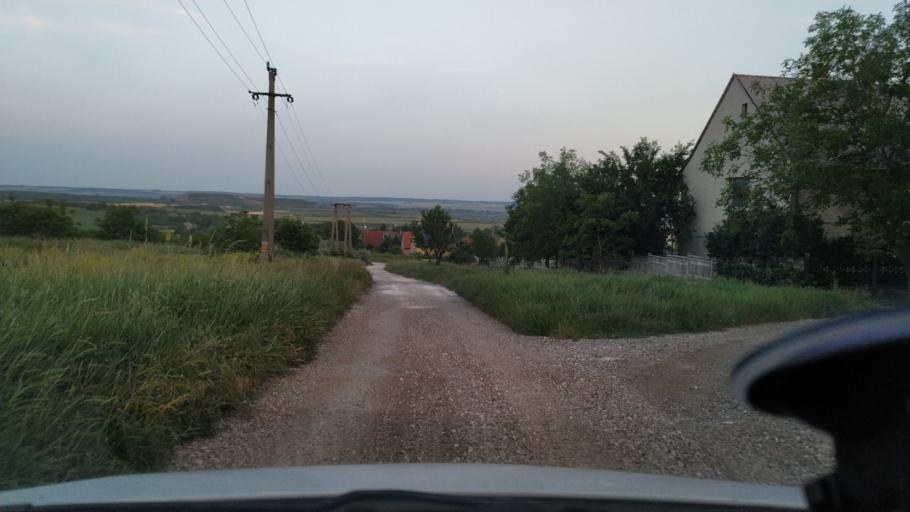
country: HU
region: Veszprem
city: Varpalota
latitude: 47.2048
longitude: 18.1828
